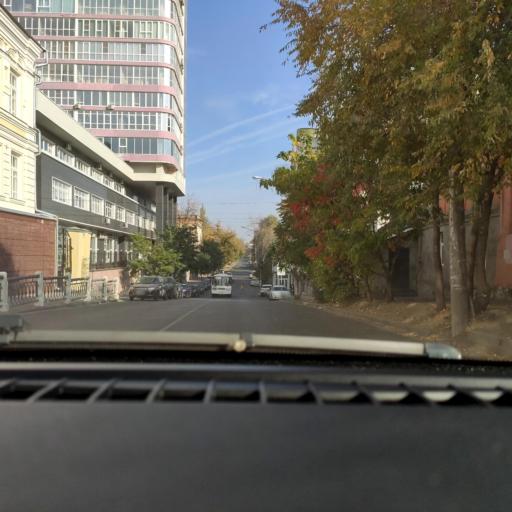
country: RU
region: Voronezj
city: Voronezh
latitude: 51.6769
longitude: 39.2179
